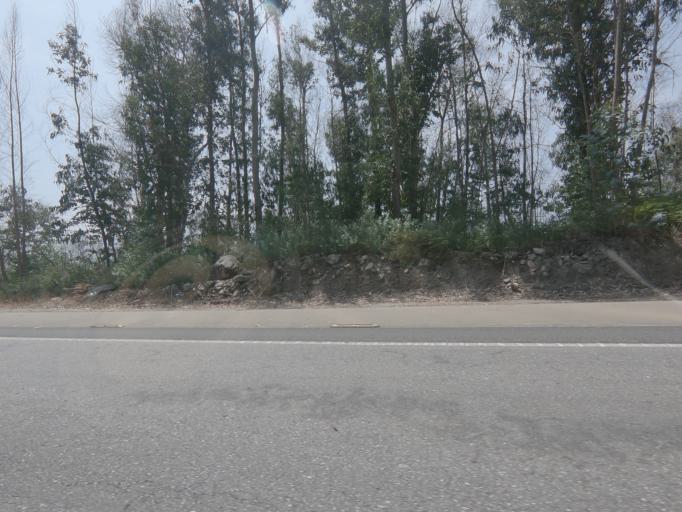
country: ES
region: Galicia
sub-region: Provincia de Pontevedra
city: A Guarda
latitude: 41.9303
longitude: -8.8818
